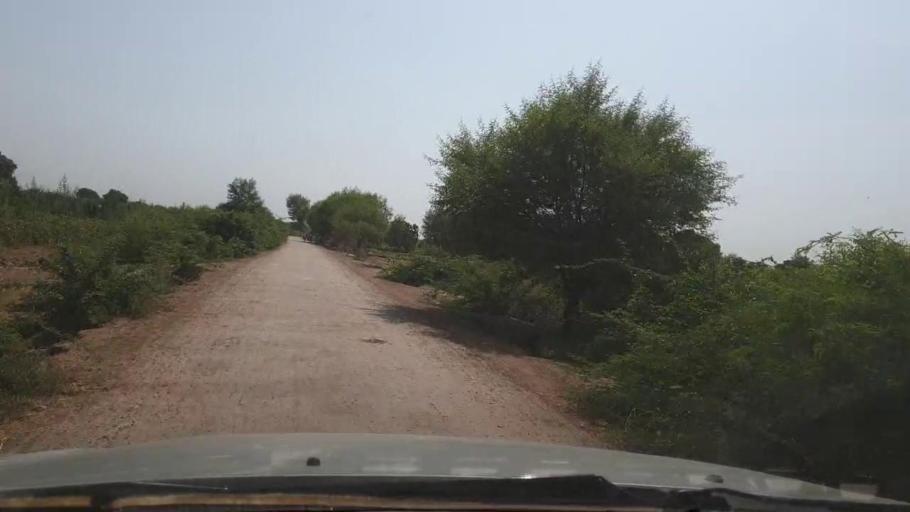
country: PK
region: Sindh
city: Tando Ghulam Ali
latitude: 25.1563
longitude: 68.8950
